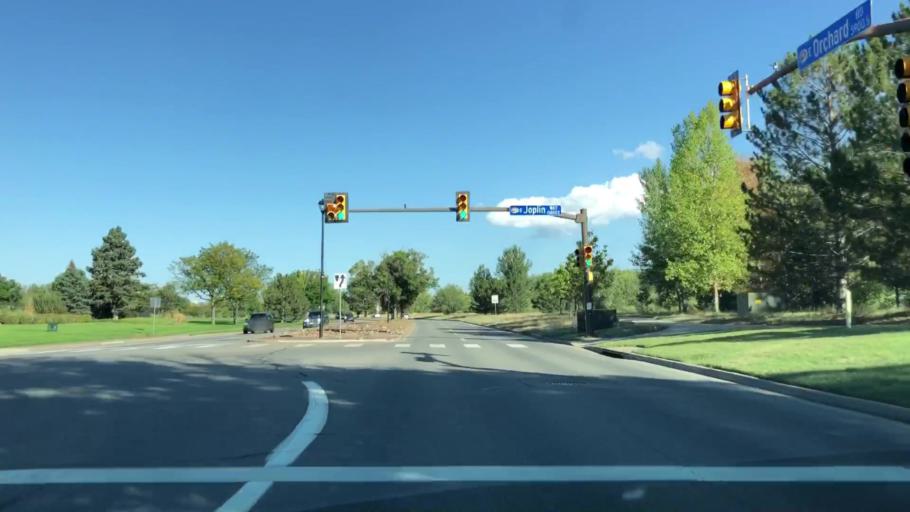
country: US
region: Colorado
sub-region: Arapahoe County
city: Dove Valley
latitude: 39.6108
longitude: -104.8052
